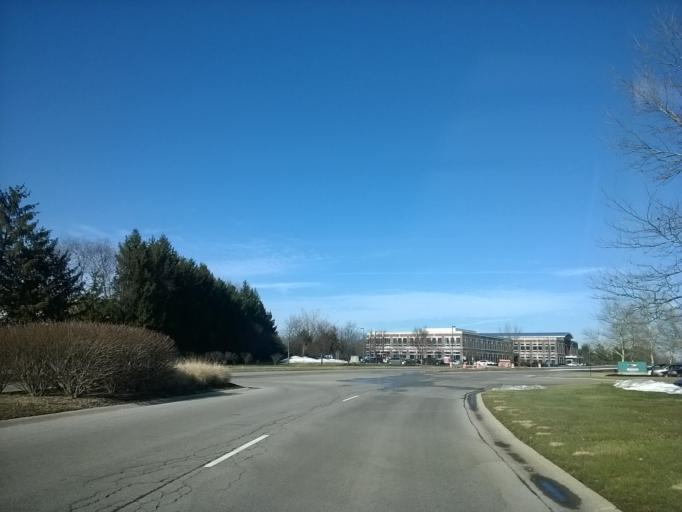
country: US
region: Indiana
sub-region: Marion County
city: Meridian Hills
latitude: 39.9346
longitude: -86.1629
